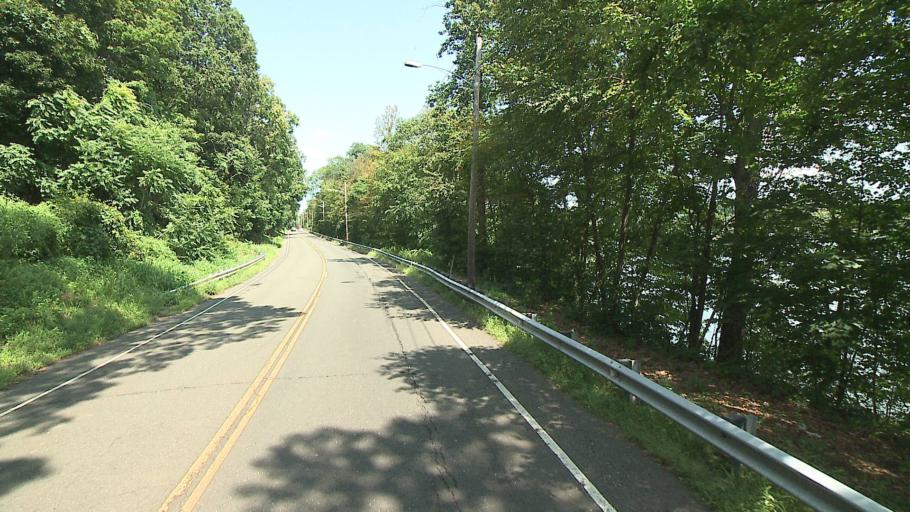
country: US
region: Connecticut
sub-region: New Haven County
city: City of Milford (balance)
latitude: 41.2329
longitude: -73.1092
